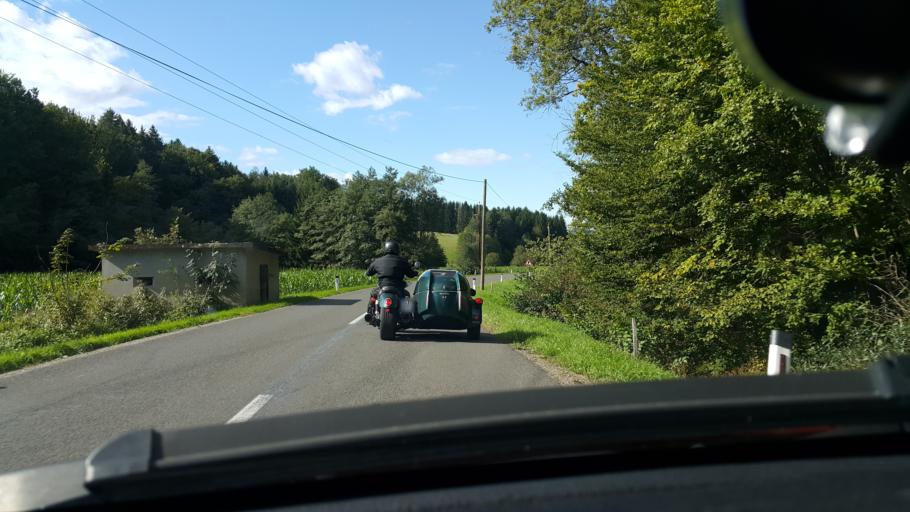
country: AT
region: Styria
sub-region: Politischer Bezirk Leibnitz
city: Leutschach
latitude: 46.6525
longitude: 15.4872
